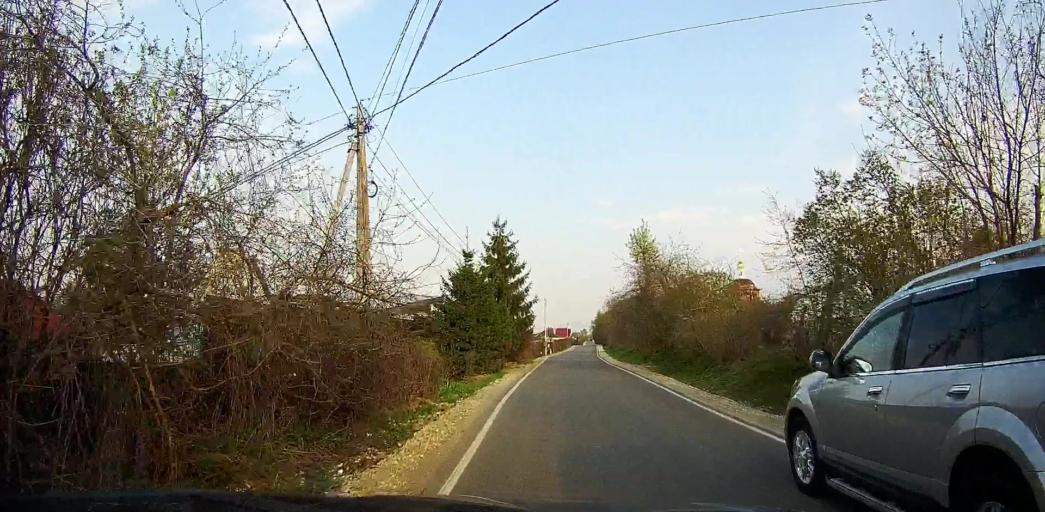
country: RU
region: Moskovskaya
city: Andreyevskoye
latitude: 55.5577
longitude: 37.9176
